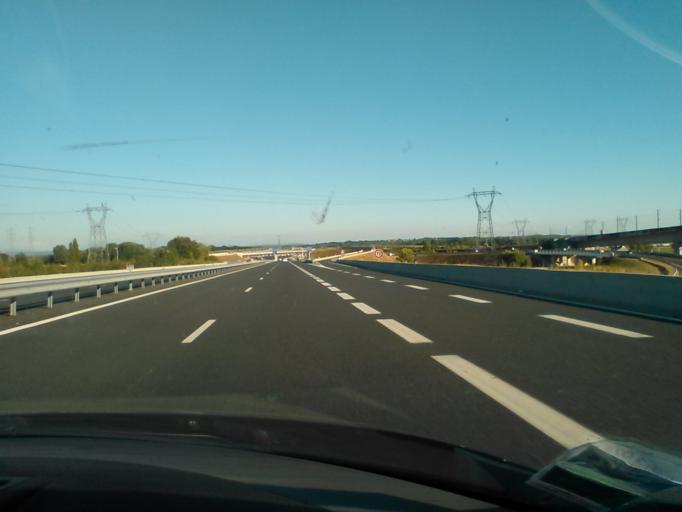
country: FR
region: Rhone-Alpes
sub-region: Departement de l'Ain
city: La Boisse
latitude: 45.8334
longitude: 5.0241
